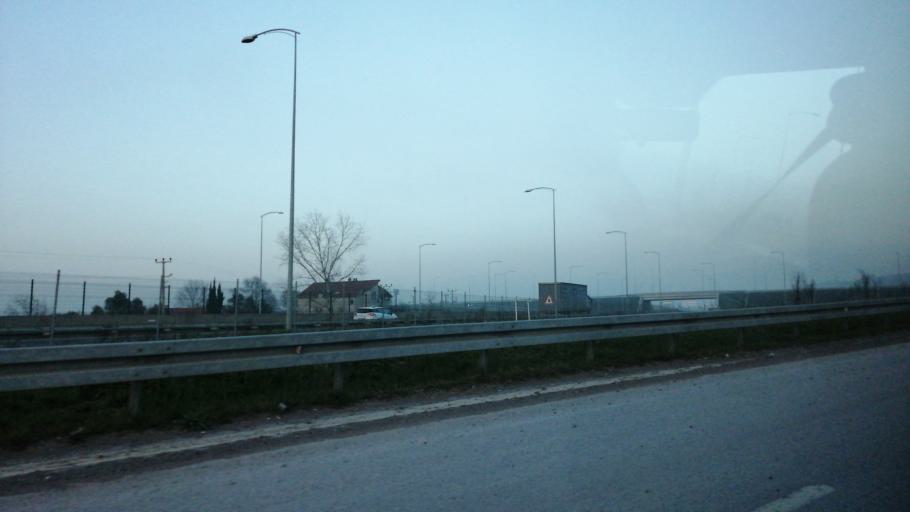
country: TR
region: Yalova
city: Altinova
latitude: 40.6899
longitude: 29.4673
